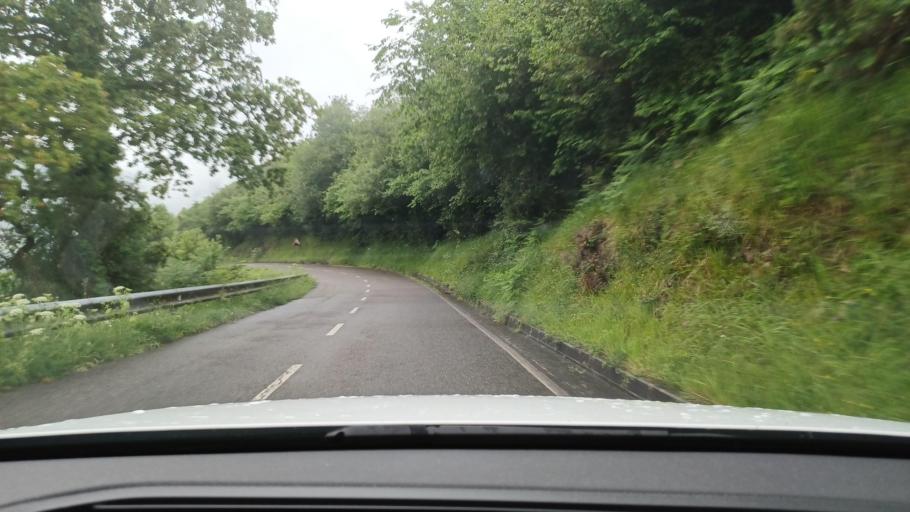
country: ES
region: Asturias
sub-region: Province of Asturias
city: Proaza
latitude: 43.2907
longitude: -5.9681
